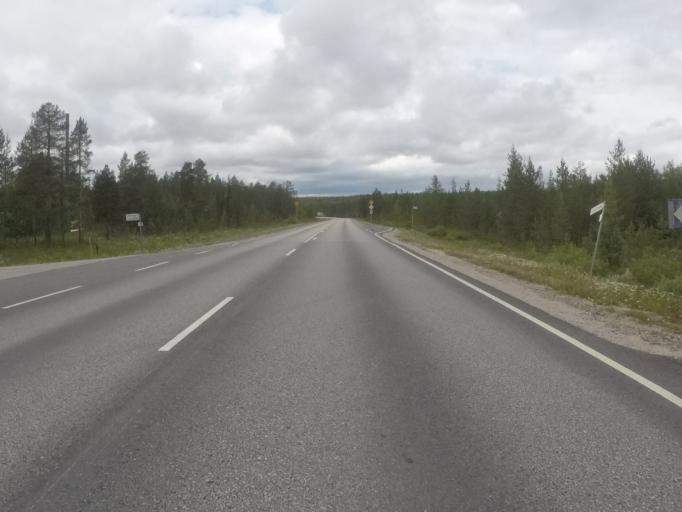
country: FI
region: Lapland
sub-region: Tunturi-Lappi
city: Muonio
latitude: 67.9858
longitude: 23.6457
